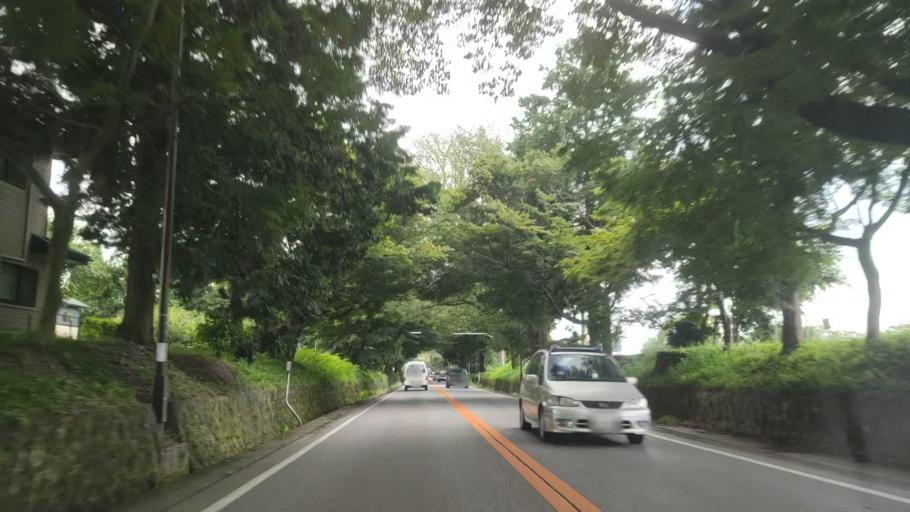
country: JP
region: Tochigi
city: Utsunomiya-shi
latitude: 36.6324
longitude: 139.8507
